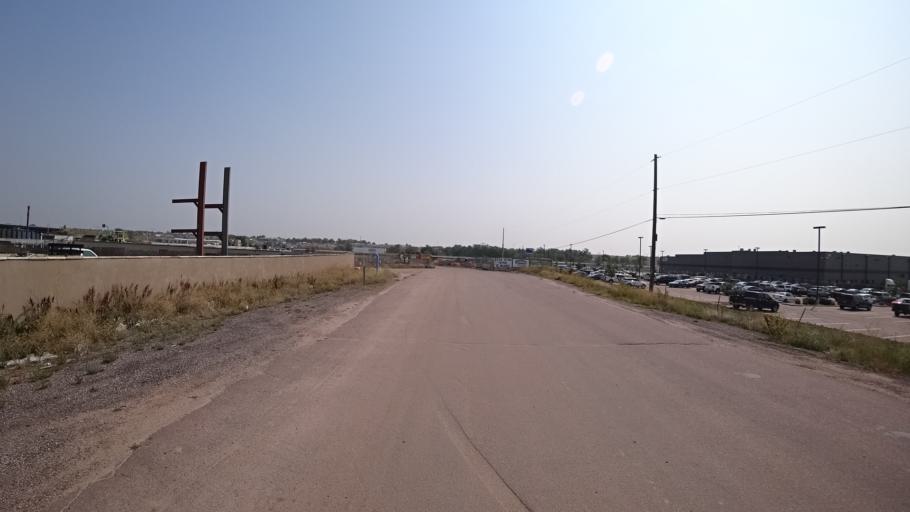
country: US
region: Colorado
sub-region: El Paso County
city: Cimarron Hills
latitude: 38.8357
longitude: -104.7238
